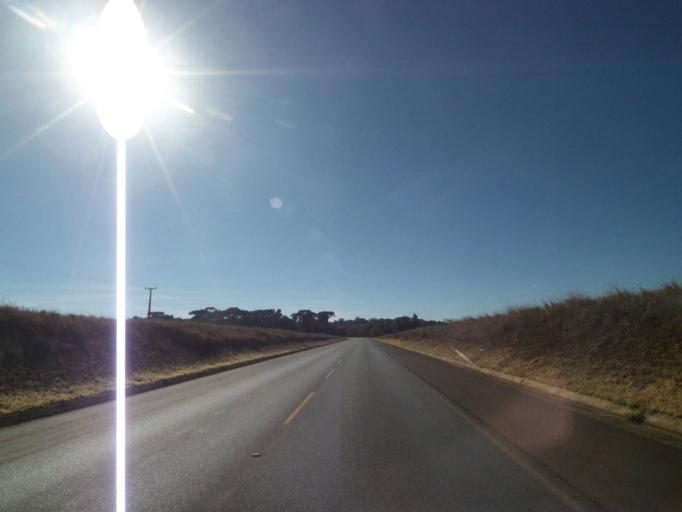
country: BR
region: Parana
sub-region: Tibagi
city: Tibagi
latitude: -24.4280
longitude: -50.4019
